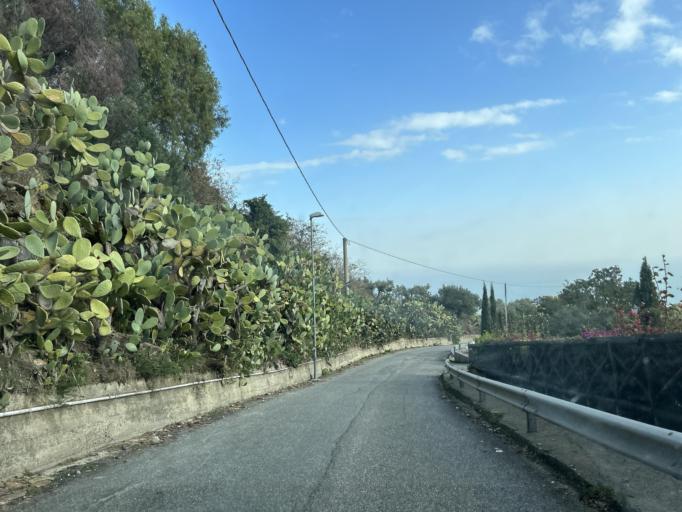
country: IT
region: Calabria
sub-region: Provincia di Catanzaro
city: Montepaone
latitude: 38.7196
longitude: 16.5042
